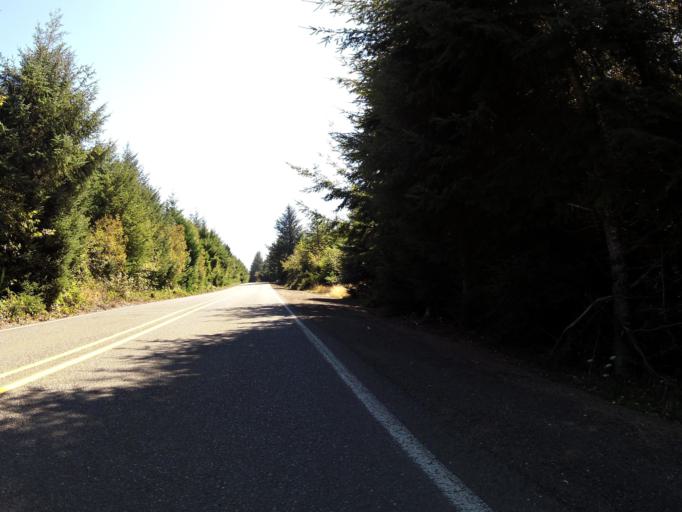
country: US
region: Oregon
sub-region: Coos County
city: Barview
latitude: 43.2652
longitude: -124.3445
